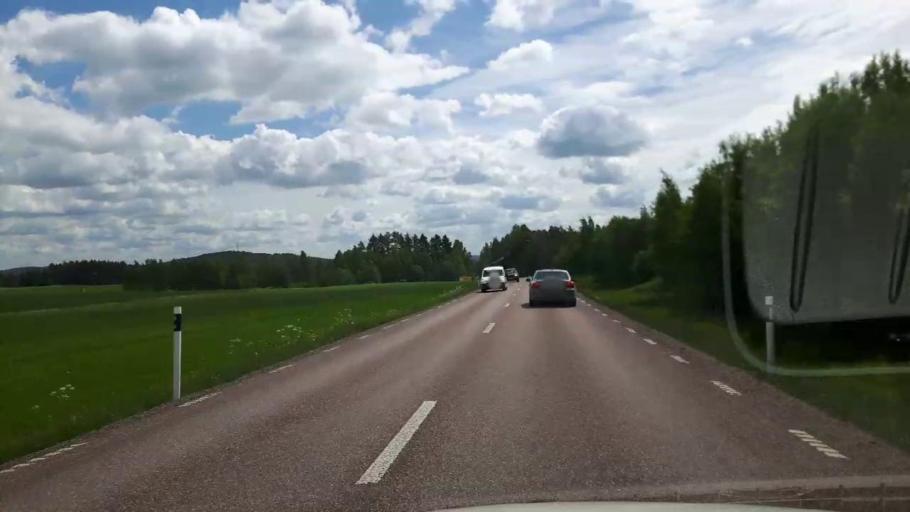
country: SE
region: Dalarna
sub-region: Saters Kommun
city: Saeter
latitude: 60.4249
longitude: 15.8394
